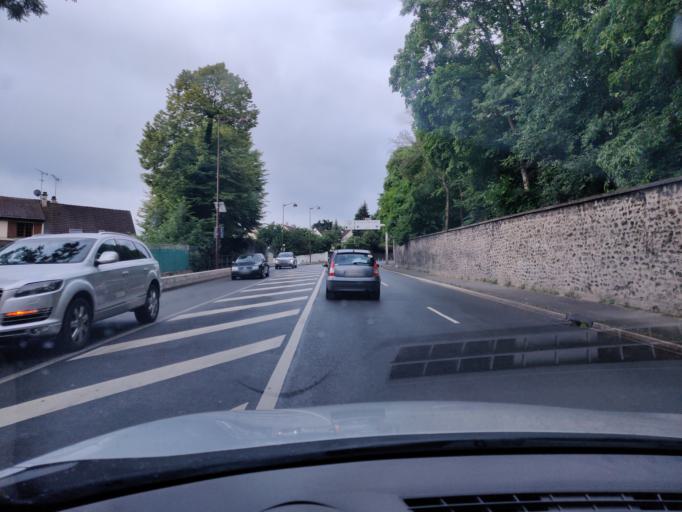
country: FR
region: Ile-de-France
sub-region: Departement de l'Essonne
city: Juvisy-sur-Orge
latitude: 48.6679
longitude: 2.3768
